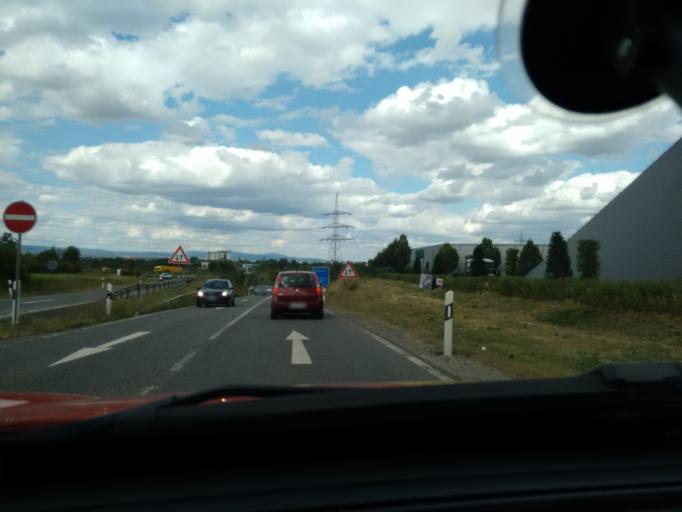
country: DE
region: Rheinland-Pfalz
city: Mainz
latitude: 49.9659
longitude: 8.2551
